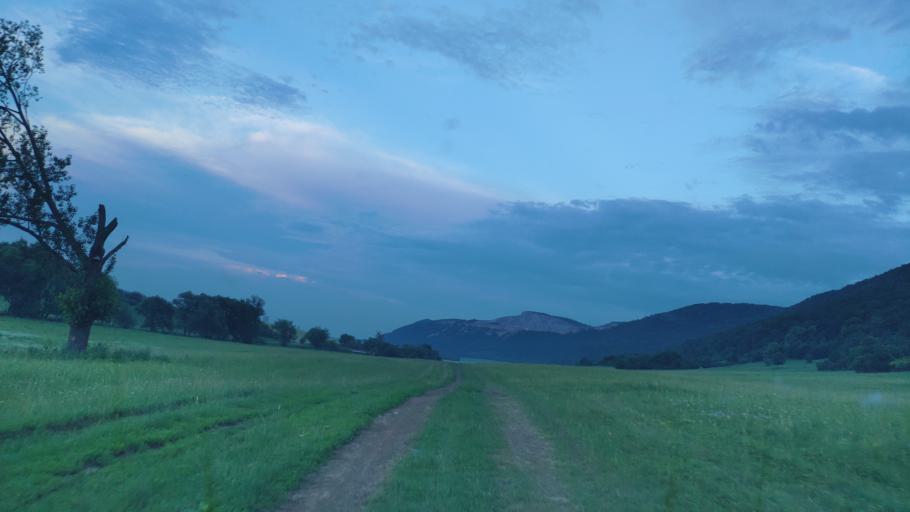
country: SK
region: Kosicky
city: Medzev
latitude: 48.5833
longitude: 20.7714
